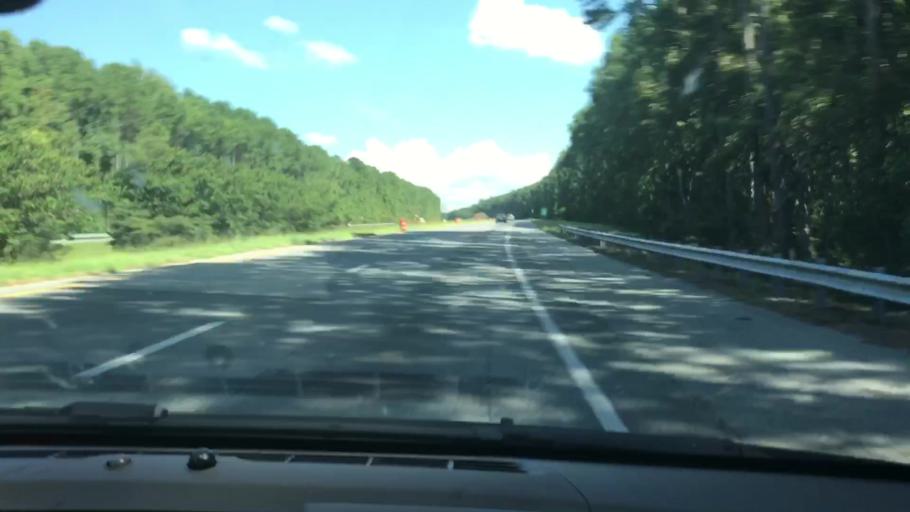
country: US
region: Georgia
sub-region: Harris County
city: Hamilton
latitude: 32.7243
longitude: -85.0191
